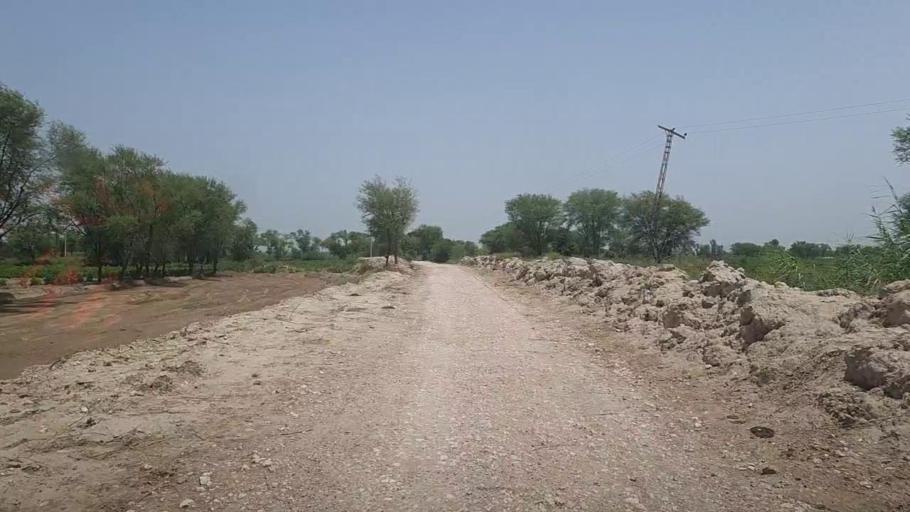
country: PK
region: Sindh
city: Pad Idan
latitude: 26.8456
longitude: 68.2945
